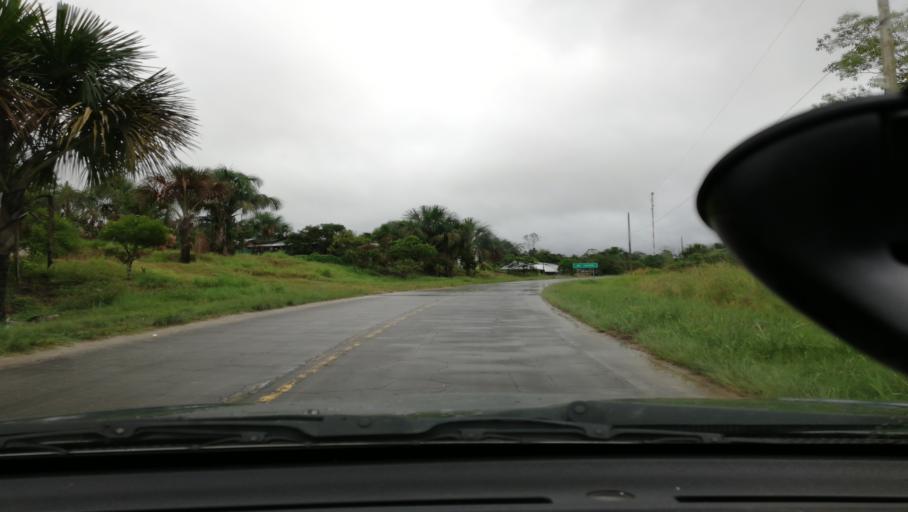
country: PE
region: Loreto
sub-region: Provincia de Loreto
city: Nauta
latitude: -4.2341
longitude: -73.4884
